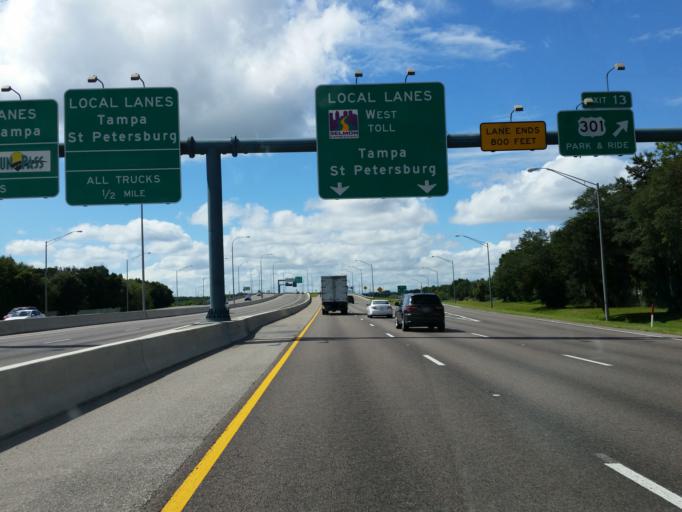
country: US
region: Florida
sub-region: Hillsborough County
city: Palm River-Clair Mel
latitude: 27.9298
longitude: -82.3458
